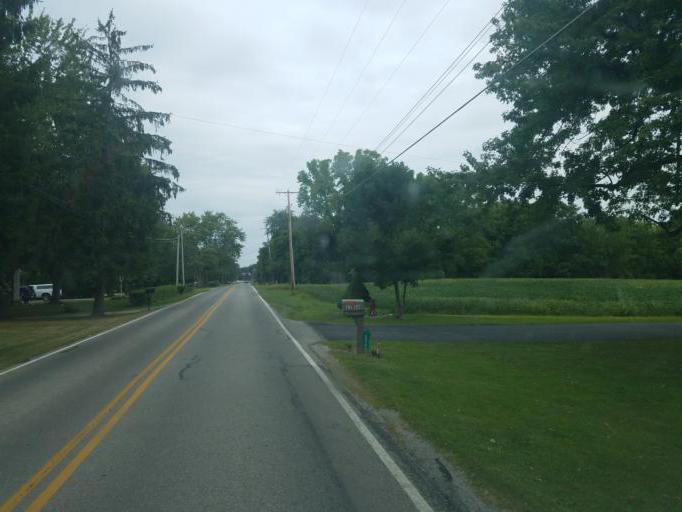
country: US
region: Ohio
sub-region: Marion County
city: Marion
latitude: 40.5450
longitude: -83.1368
